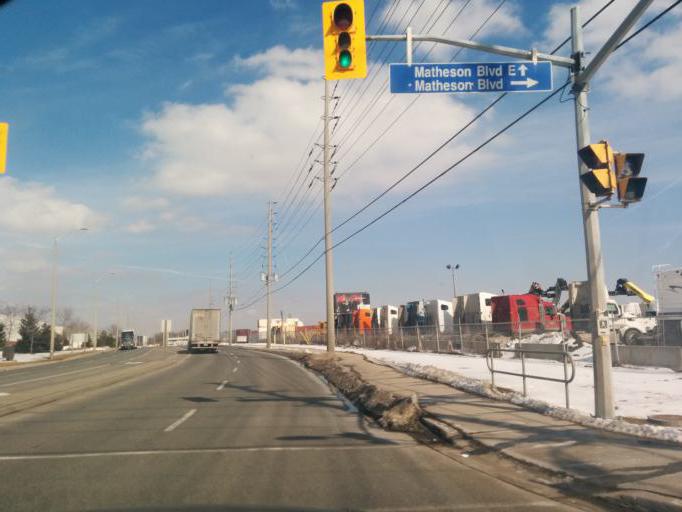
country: CA
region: Ontario
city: Etobicoke
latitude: 43.6437
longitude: -79.6282
